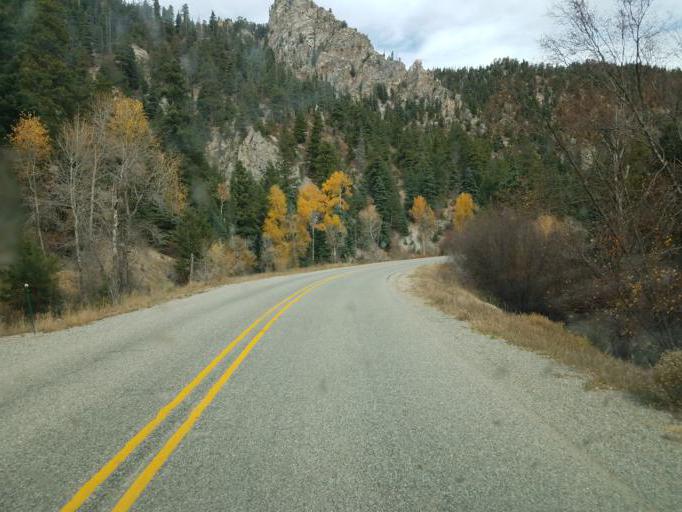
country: US
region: New Mexico
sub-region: Taos County
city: Arroyo Seco
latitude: 36.5579
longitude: -105.5367
